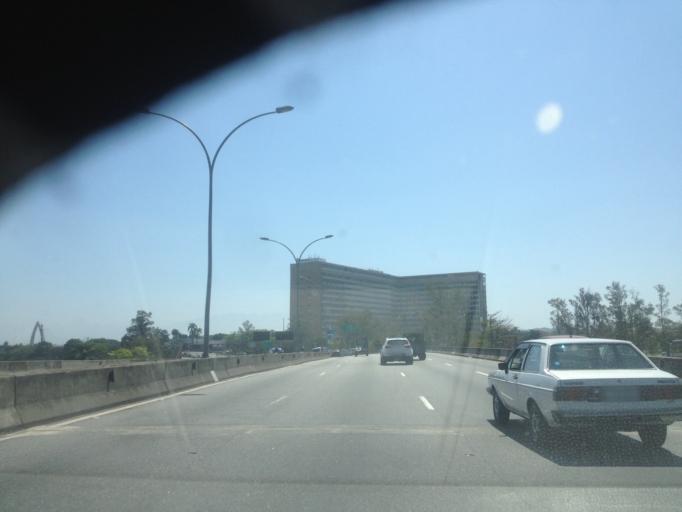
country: BR
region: Rio de Janeiro
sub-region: Rio De Janeiro
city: Rio de Janeiro
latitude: -22.8466
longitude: -43.2405
